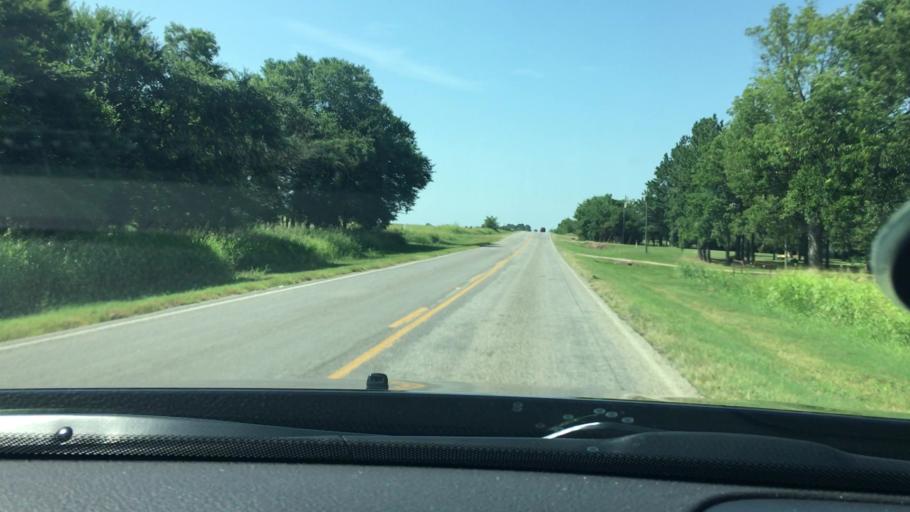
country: US
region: Oklahoma
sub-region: Johnston County
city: Tishomingo
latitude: 34.2894
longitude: -96.4248
